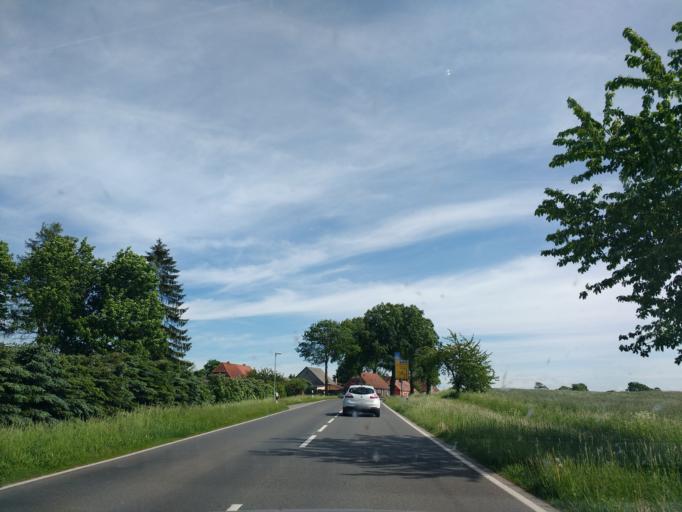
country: DE
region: Mecklenburg-Vorpommern
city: Zurow
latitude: 53.8453
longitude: 11.6440
